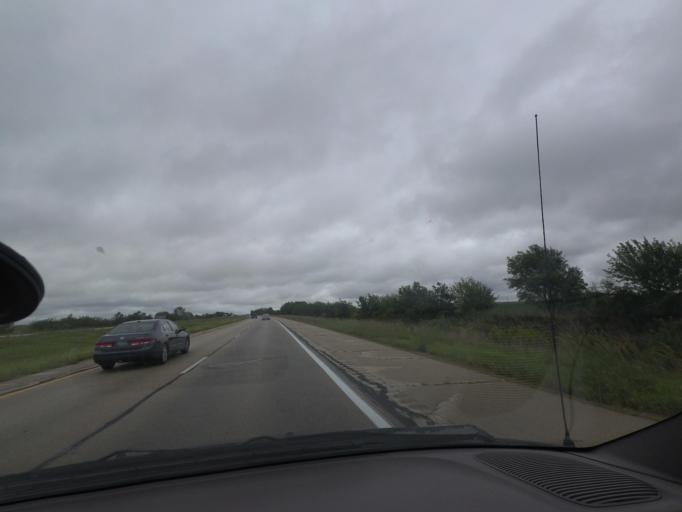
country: US
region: Illinois
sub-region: Piatt County
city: Cerro Gordo
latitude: 40.0186
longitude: -88.7205
